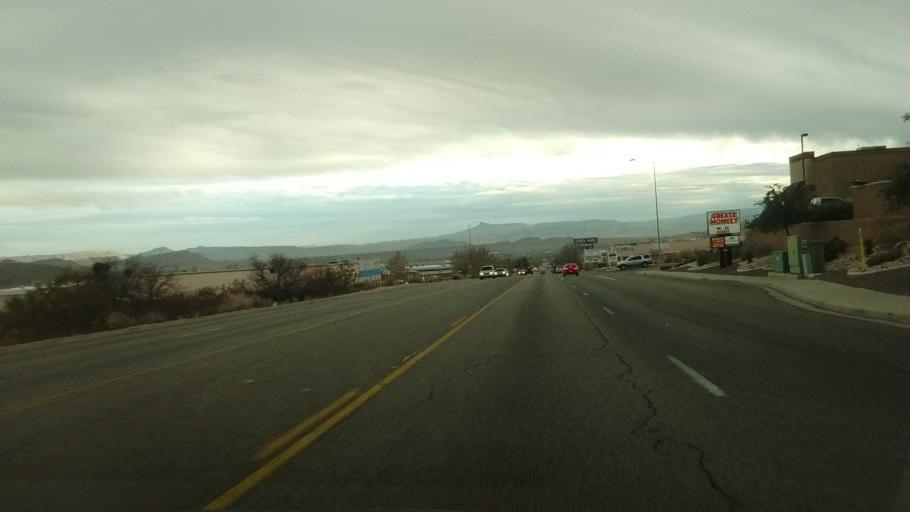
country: US
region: Utah
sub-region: Washington County
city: Washington
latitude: 37.1220
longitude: -113.5207
